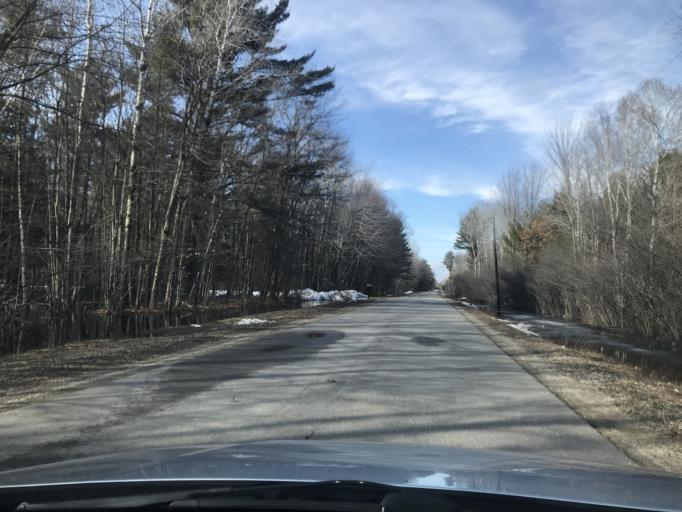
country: US
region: Wisconsin
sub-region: Marinette County
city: Marinette
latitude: 45.0320
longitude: -87.6676
